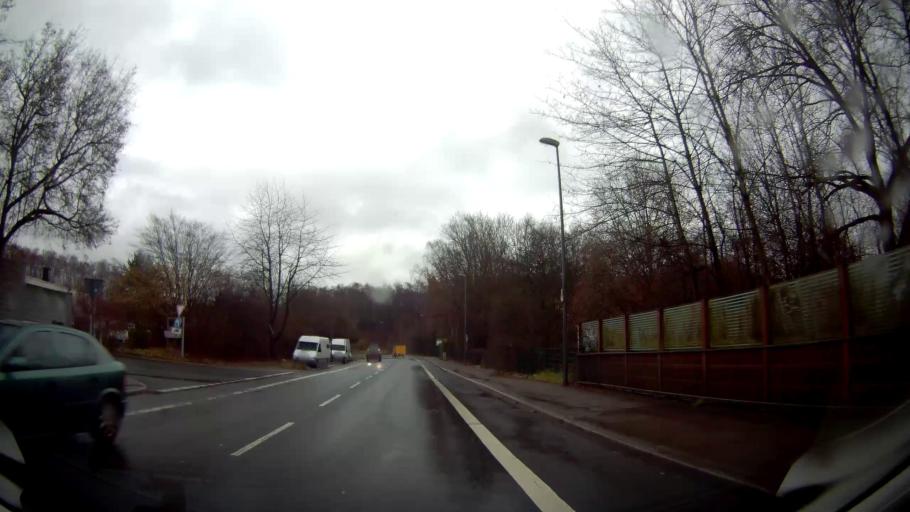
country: DE
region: North Rhine-Westphalia
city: Bochum-Hordel
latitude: 51.5151
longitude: 7.2024
